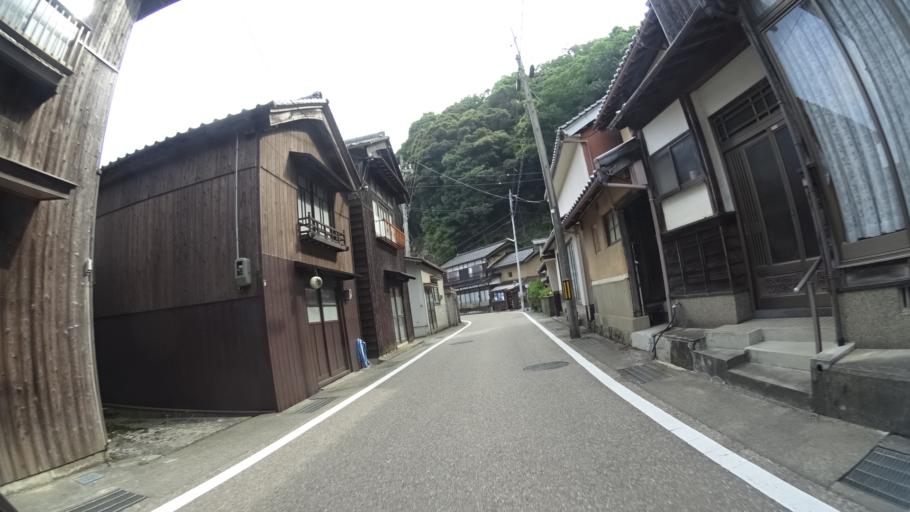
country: JP
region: Kyoto
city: Miyazu
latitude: 35.6710
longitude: 135.2835
